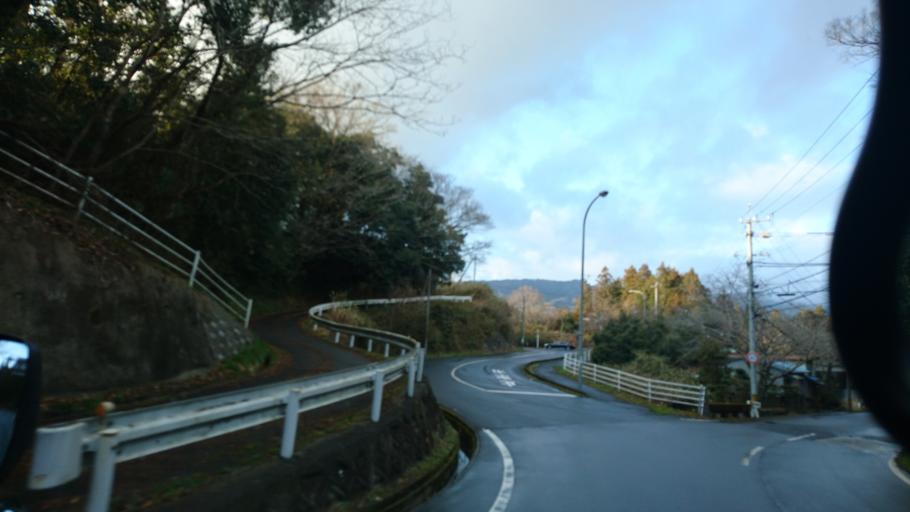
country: JP
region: Mie
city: Ueno-ebisumachi
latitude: 34.7612
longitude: 136.0555
